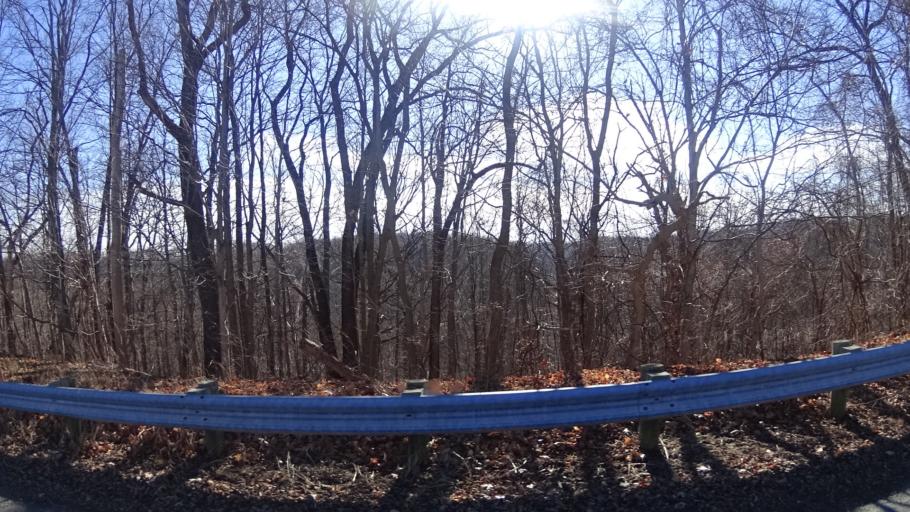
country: US
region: Ohio
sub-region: Lorain County
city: Vermilion
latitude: 41.3620
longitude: -82.3374
